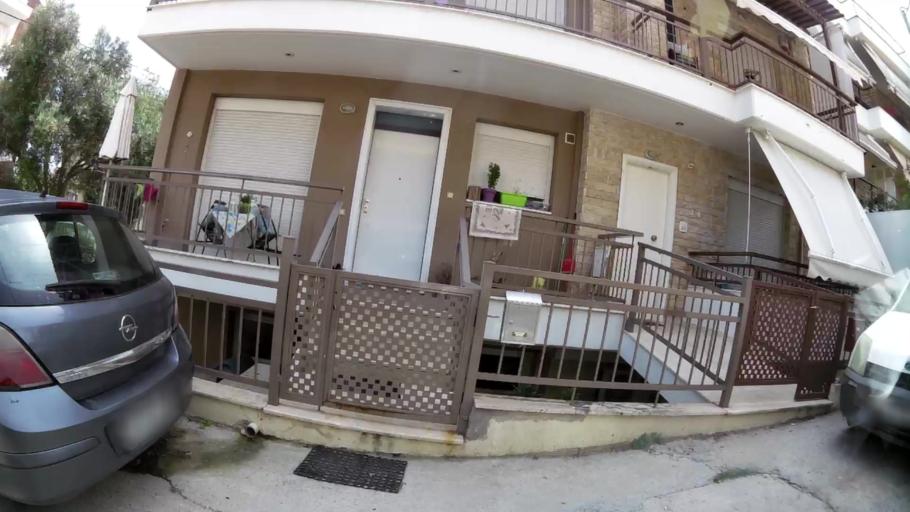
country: GR
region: Central Macedonia
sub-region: Nomos Thessalonikis
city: Pylaia
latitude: 40.5945
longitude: 22.9789
